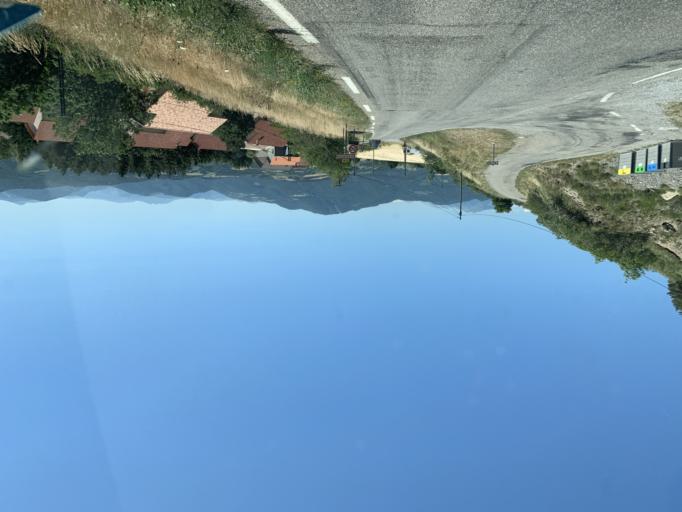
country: FR
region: Provence-Alpes-Cote d'Azur
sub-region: Departement des Hautes-Alpes
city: La Batie-Neuve
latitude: 44.5960
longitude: 6.1505
